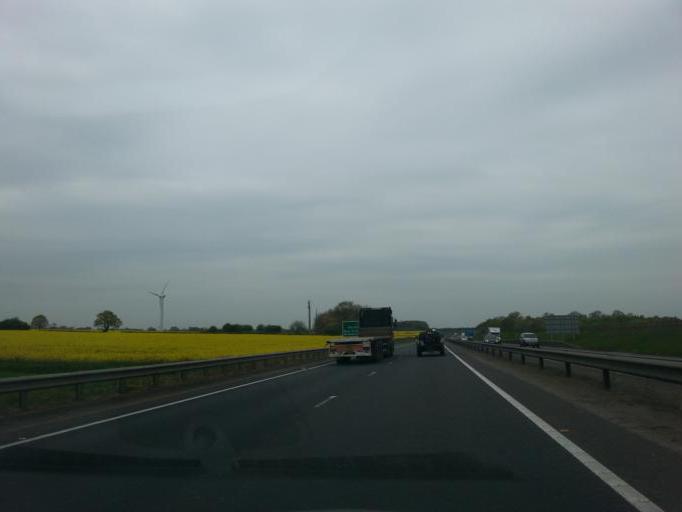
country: GB
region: England
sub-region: Suffolk
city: Stowmarket
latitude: 52.2099
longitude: 0.9668
